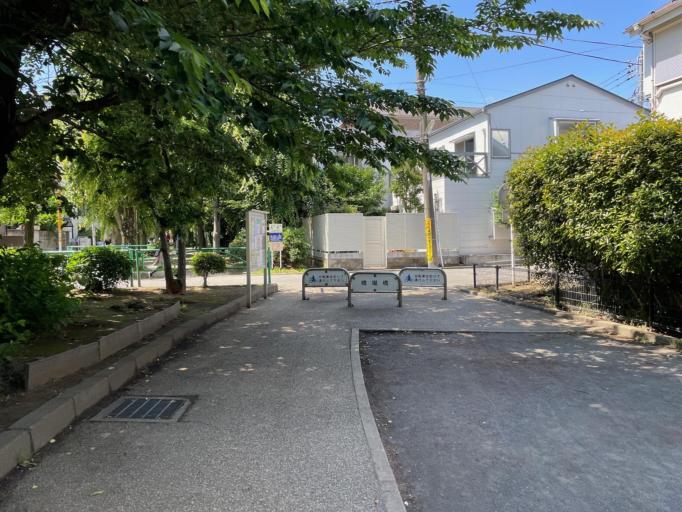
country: JP
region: Tokyo
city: Tokyo
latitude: 35.6502
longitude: 139.6308
